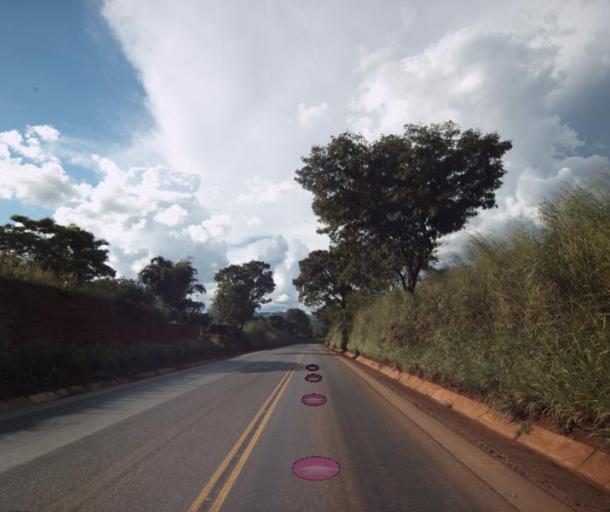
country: BR
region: Goias
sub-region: Rialma
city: Rialma
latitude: -15.3167
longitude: -49.5724
